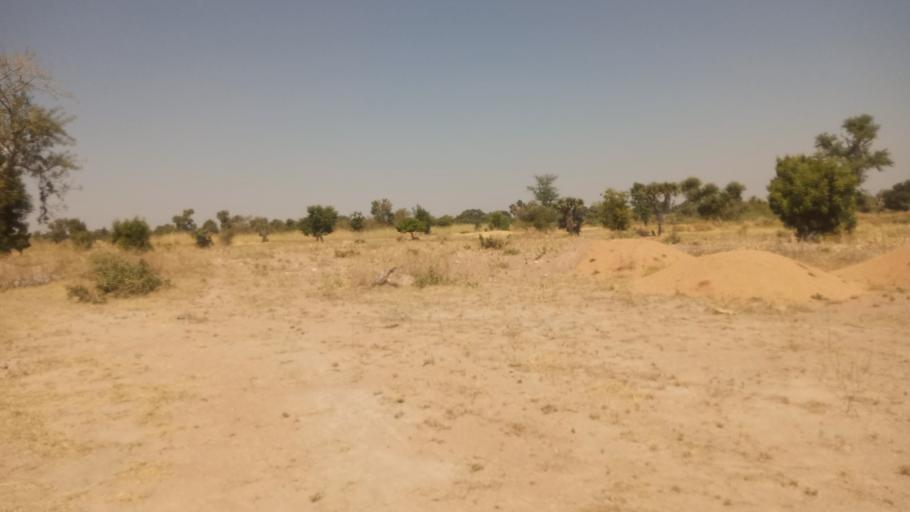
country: NG
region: Adamawa
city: Mayo Belwa
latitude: 9.0931
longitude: 12.0244
